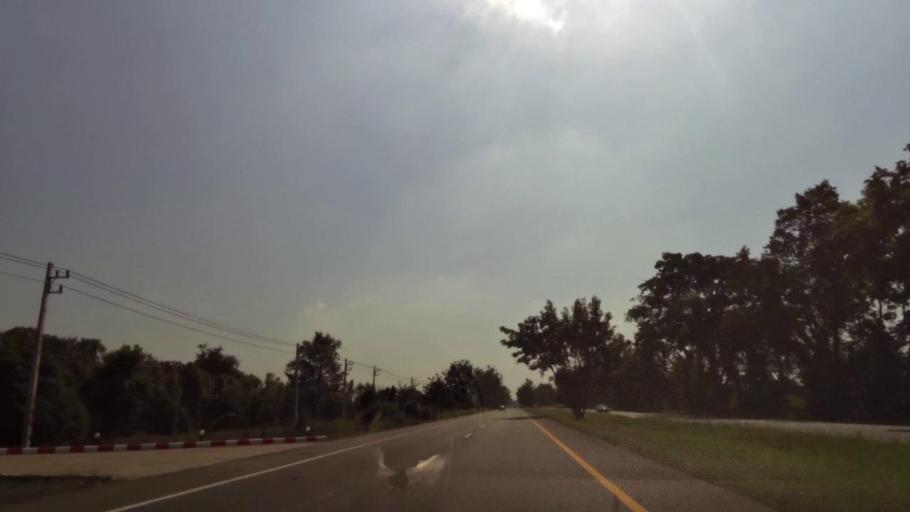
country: TH
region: Phichit
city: Bueng Na Rang
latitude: 16.2047
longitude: 100.1277
